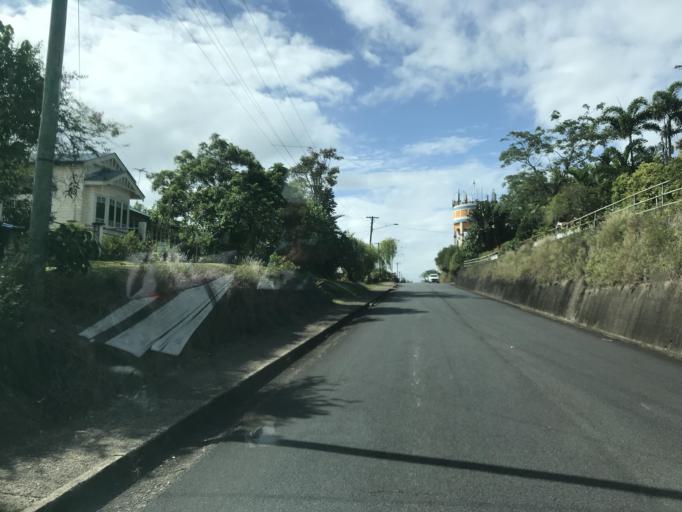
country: AU
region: Queensland
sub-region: Cassowary Coast
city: Innisfail
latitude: -17.5268
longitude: 146.0343
